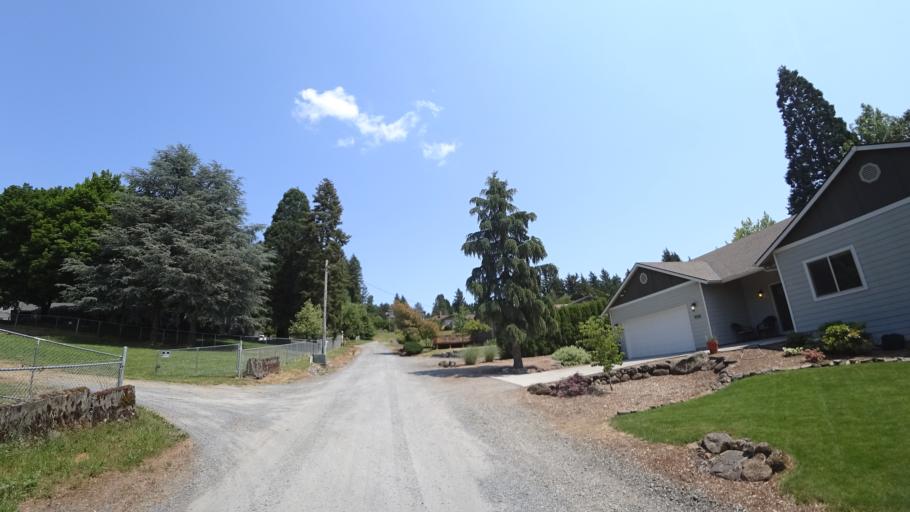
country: US
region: Oregon
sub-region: Multnomah County
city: Lents
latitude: 45.4513
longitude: -122.5654
